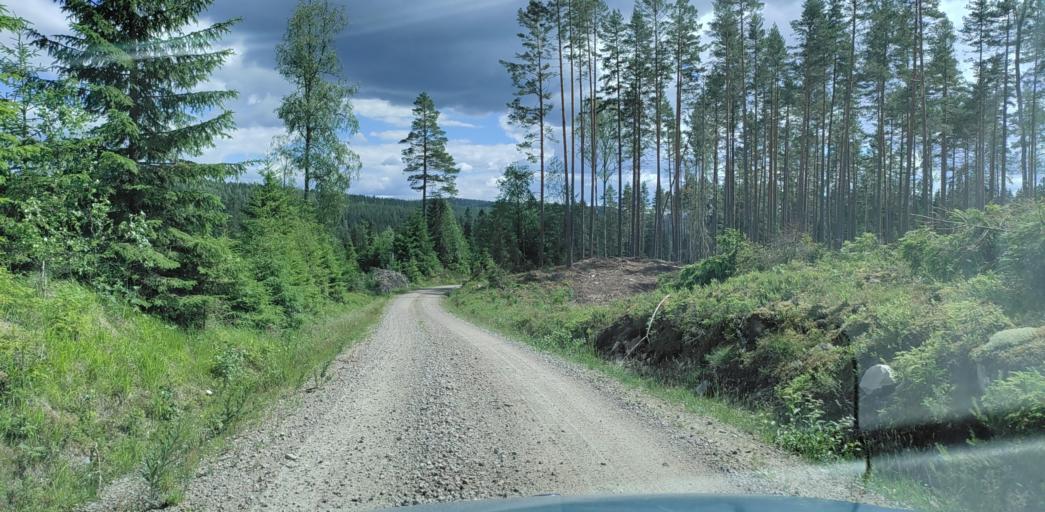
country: SE
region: Vaermland
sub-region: Hagfors Kommun
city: Ekshaerad
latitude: 60.0449
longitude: 13.3102
